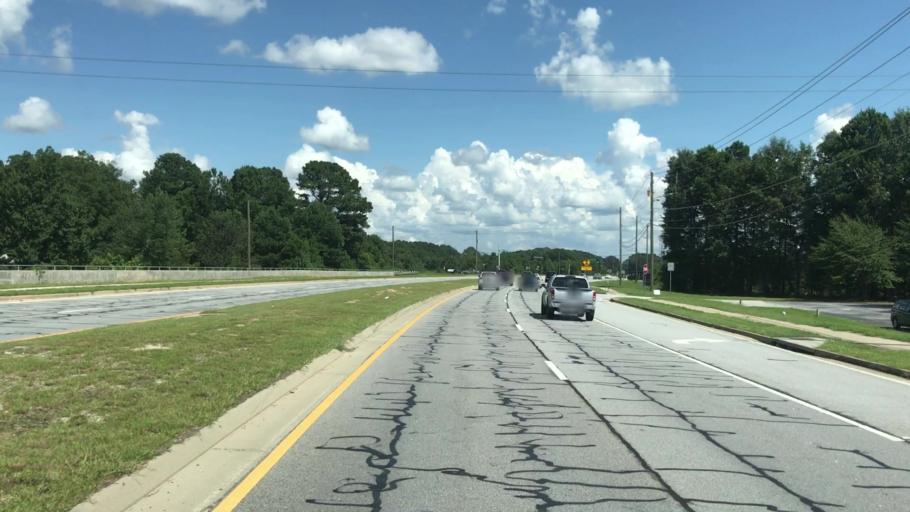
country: US
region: Georgia
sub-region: Walton County
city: Loganville
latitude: 33.8688
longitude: -83.9132
